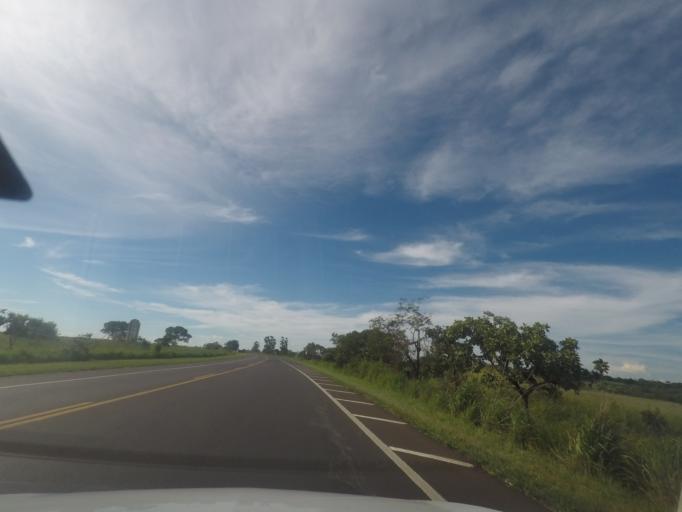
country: BR
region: Minas Gerais
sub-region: Monte Alegre De Minas
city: Monte Alegre de Minas
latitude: -18.9155
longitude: -49.0353
